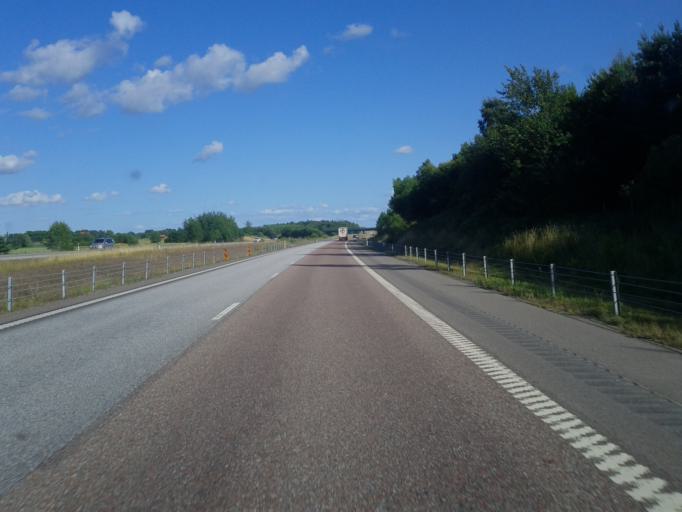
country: SE
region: Uppsala
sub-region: Enkopings Kommun
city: Dalby
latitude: 59.6068
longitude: 17.4259
